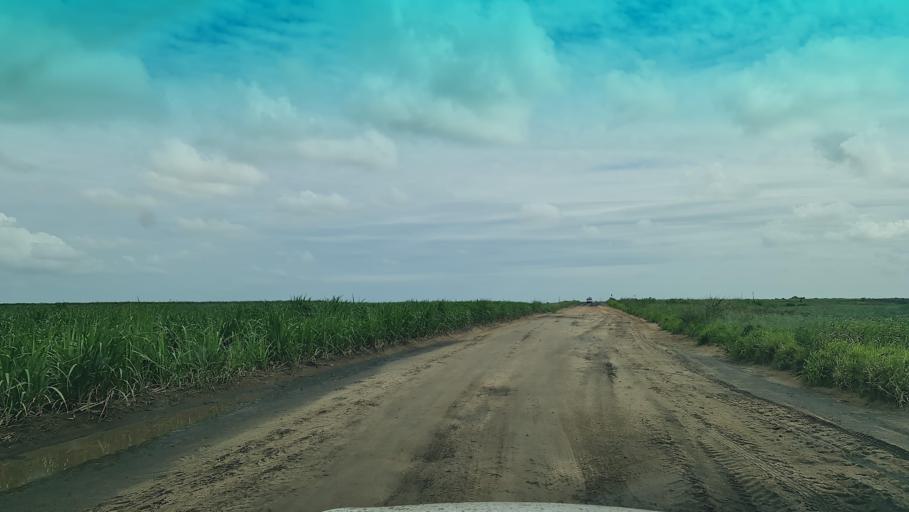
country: MZ
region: Maputo
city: Manhica
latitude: -25.4545
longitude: 32.8192
